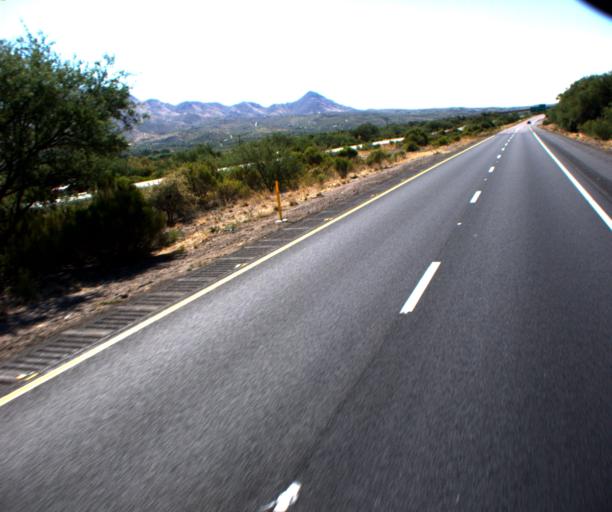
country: US
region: Arizona
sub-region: Santa Cruz County
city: Rio Rico
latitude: 31.5322
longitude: -111.0301
